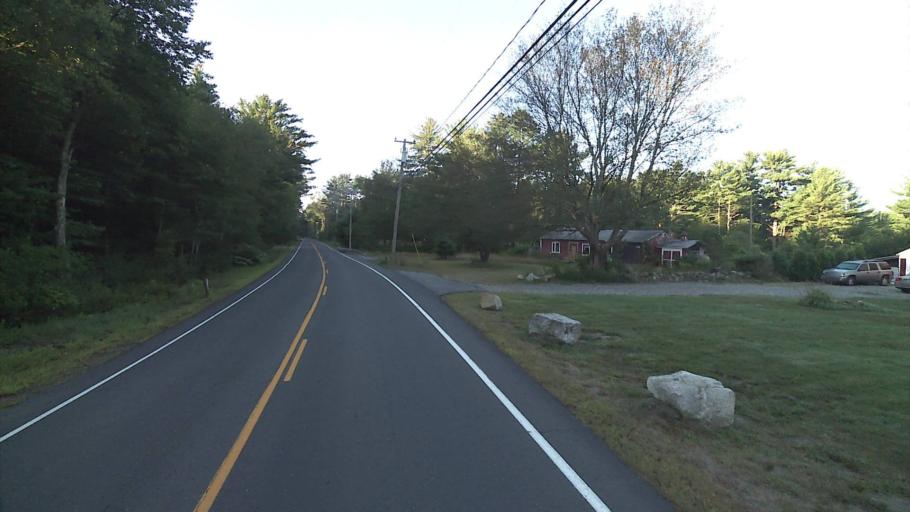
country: US
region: Connecticut
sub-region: Tolland County
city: Stafford
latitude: 42.0106
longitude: -72.3173
